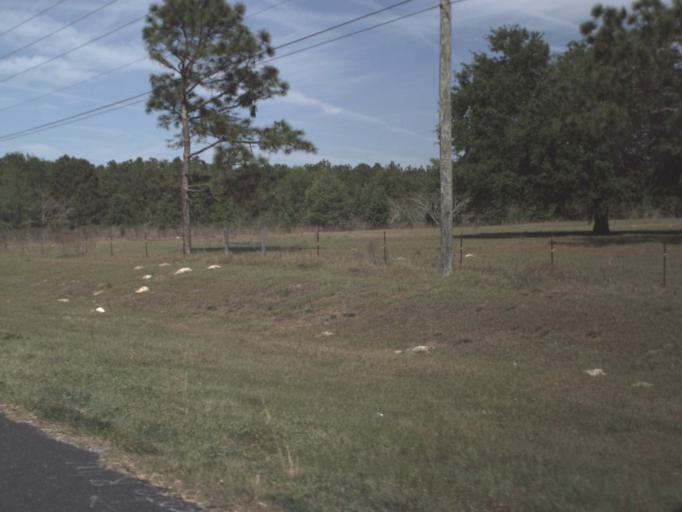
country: US
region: Florida
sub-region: Marion County
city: Belleview
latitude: 29.0259
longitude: -82.1252
